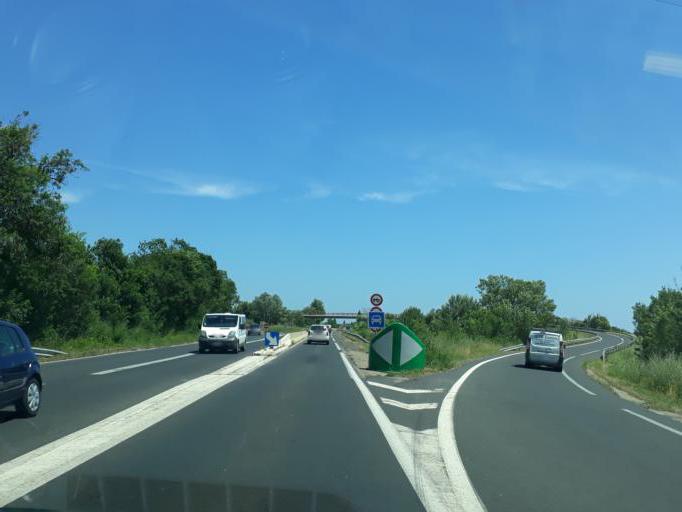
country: FR
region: Languedoc-Roussillon
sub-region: Departement de l'Herault
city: Vias
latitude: 43.3115
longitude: 3.3976
